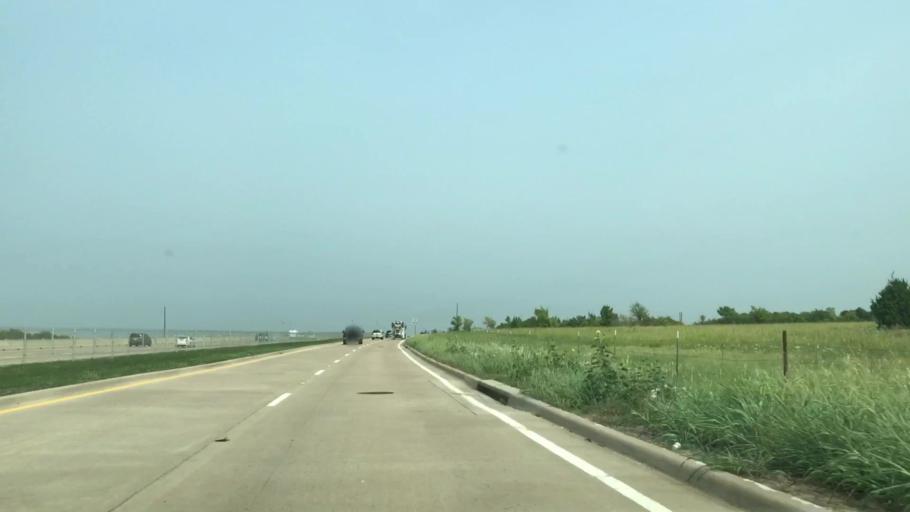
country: US
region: Texas
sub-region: Dallas County
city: Sachse
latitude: 32.9510
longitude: -96.5784
